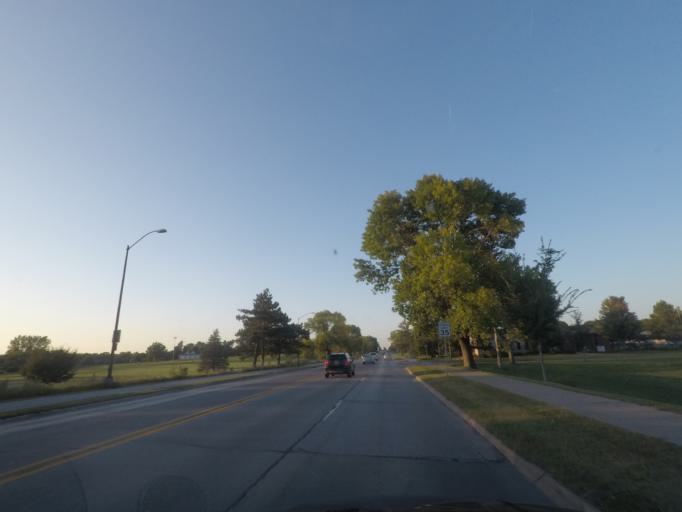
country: US
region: Iowa
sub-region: Story County
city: Ames
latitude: 42.0385
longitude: -93.6448
